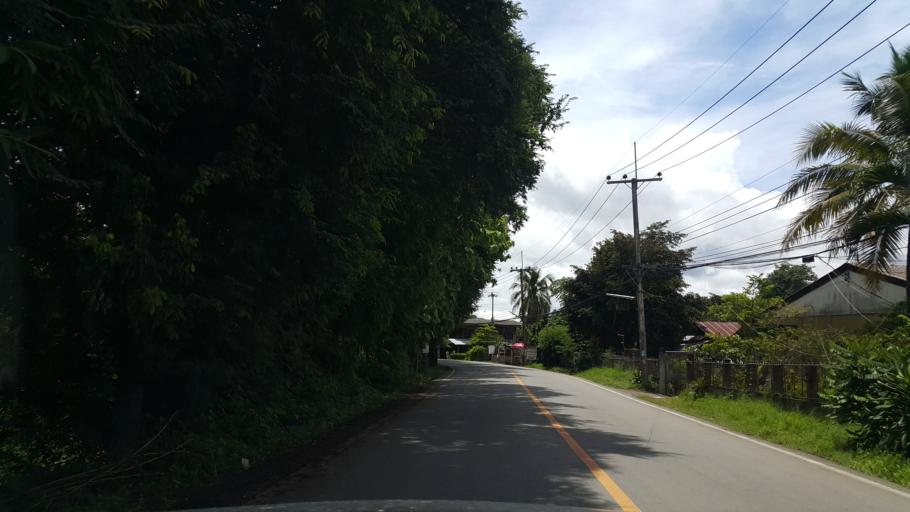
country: TH
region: Chiang Mai
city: San Kamphaeng
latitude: 18.7293
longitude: 99.1336
